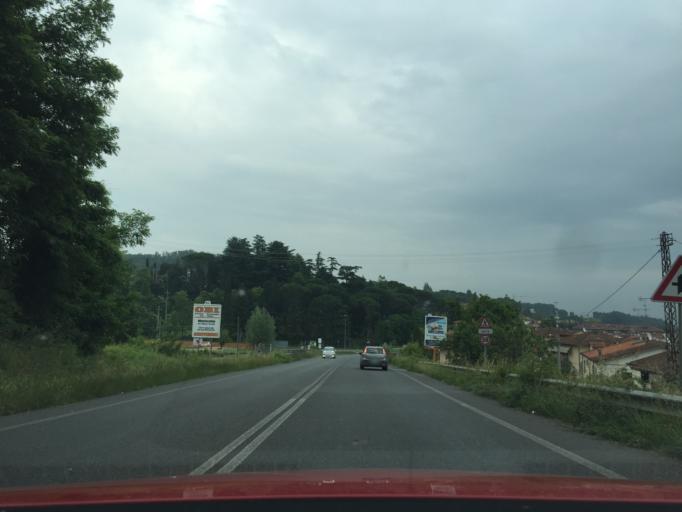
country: IT
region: Tuscany
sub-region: Provincia di Pistoia
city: Stazione Masotti
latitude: 43.9084
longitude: 10.8503
